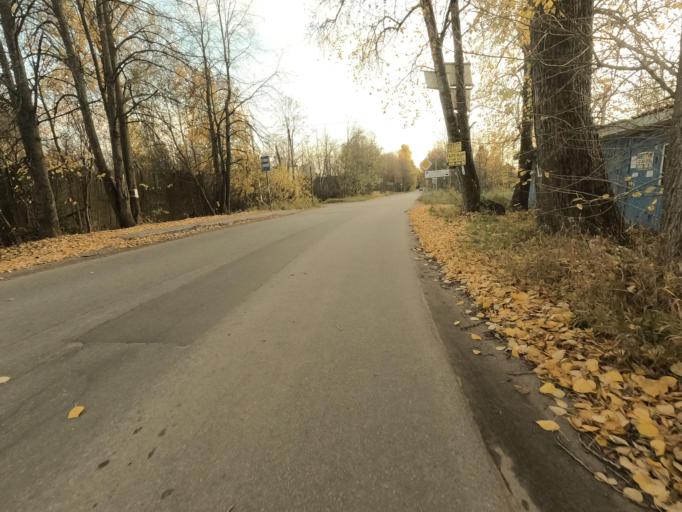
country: RU
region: St.-Petersburg
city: Beloostrov
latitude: 60.1711
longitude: 30.0135
